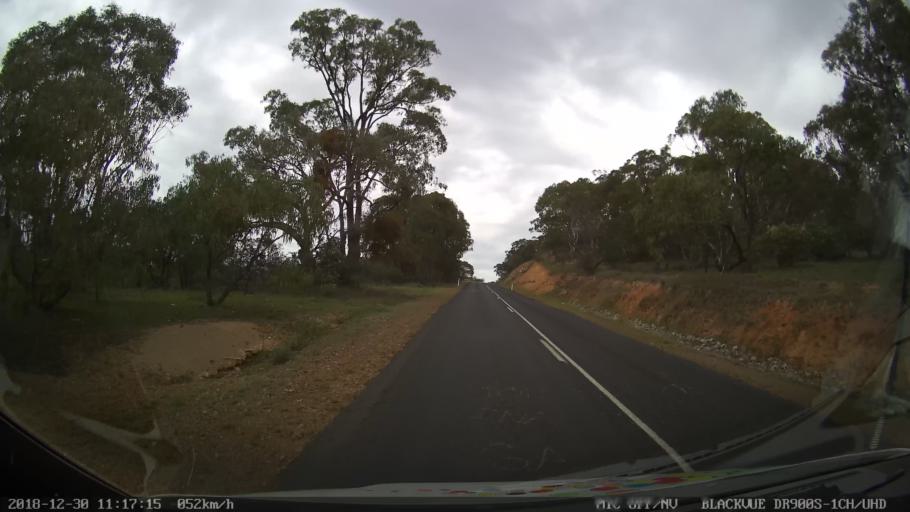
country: AU
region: New South Wales
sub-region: Snowy River
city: Jindabyne
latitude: -36.5363
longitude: 148.7001
